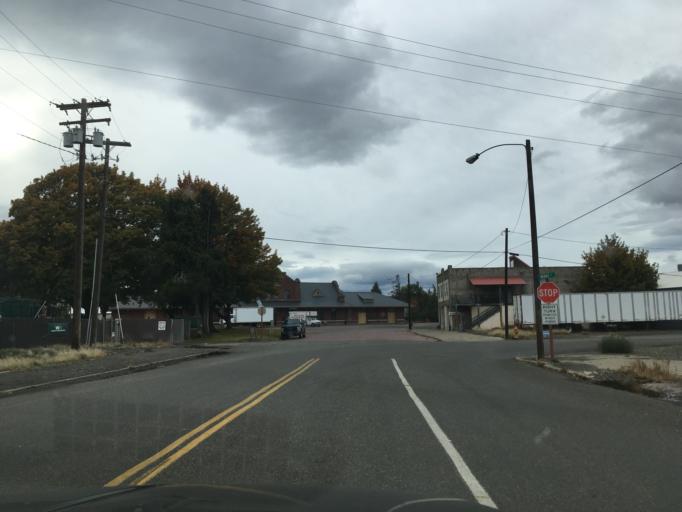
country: US
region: Washington
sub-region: Kittitas County
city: Ellensburg
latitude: 46.9943
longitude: -120.5535
